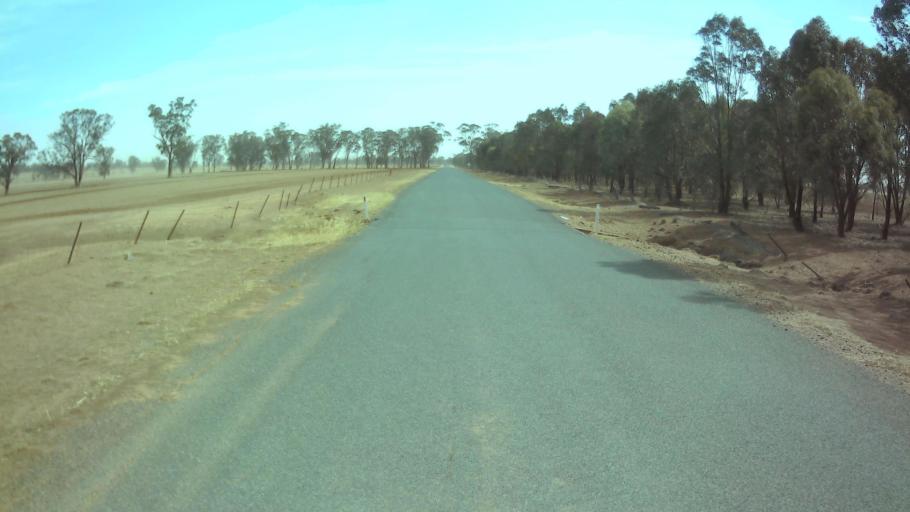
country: AU
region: New South Wales
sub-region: Weddin
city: Grenfell
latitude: -33.7186
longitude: 148.0003
